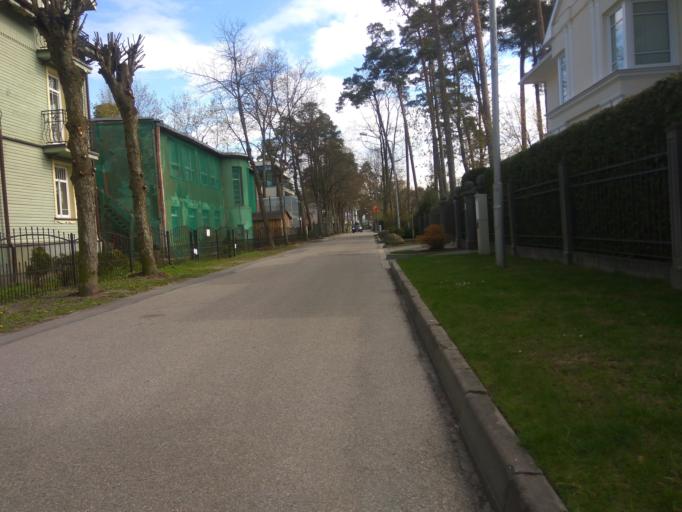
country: LV
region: Jurmala
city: Jurmala
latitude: 56.9769
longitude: 23.8101
